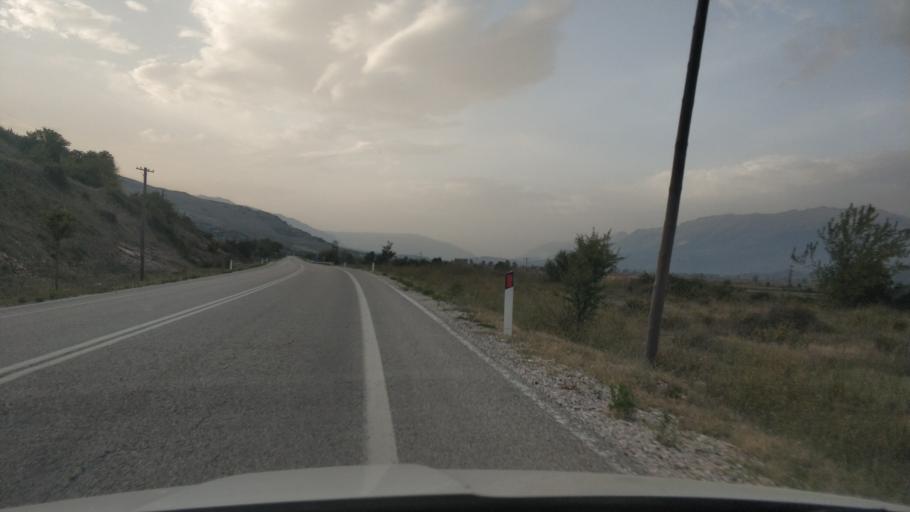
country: AL
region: Gjirokaster
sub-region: Rrethi i Gjirokastres
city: Libohove
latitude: 39.9495
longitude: 20.2572
